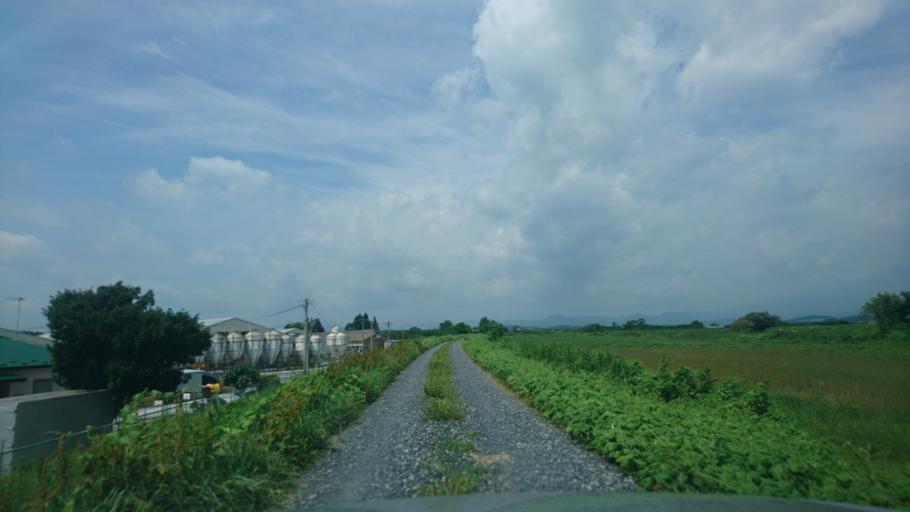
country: JP
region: Iwate
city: Ichinoseki
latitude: 38.7742
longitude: 141.0496
